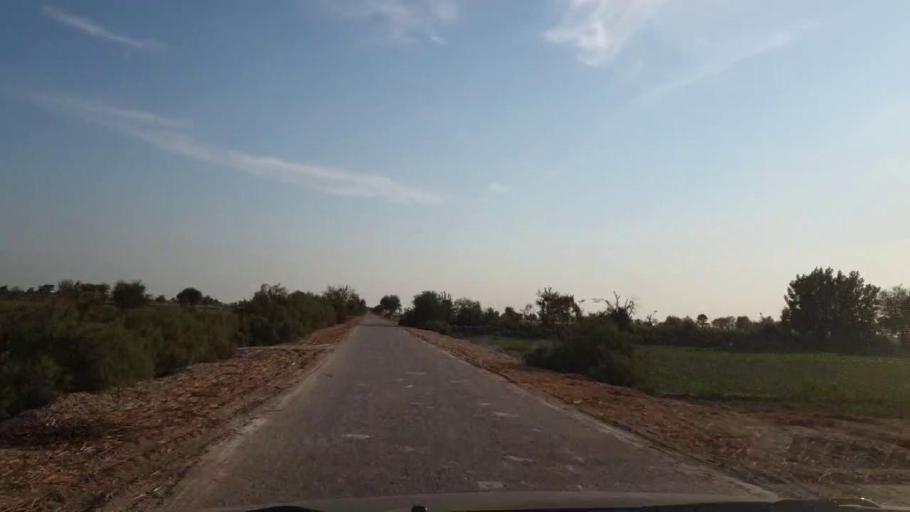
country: PK
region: Sindh
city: Khadro
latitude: 26.1997
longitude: 68.7468
